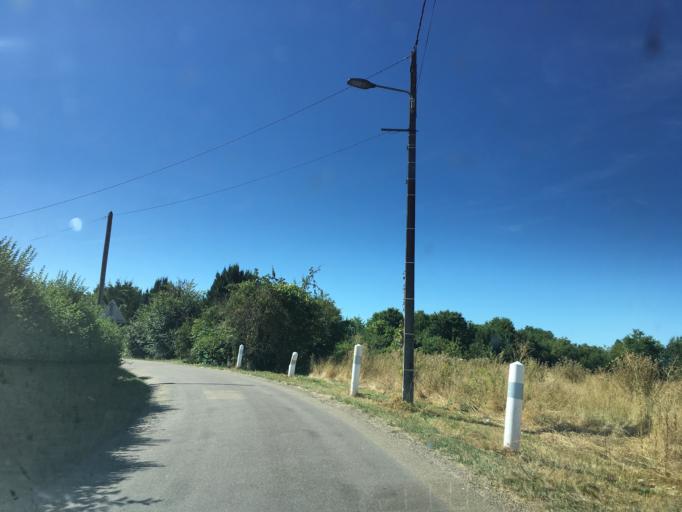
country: FR
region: Bourgogne
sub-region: Departement de l'Yonne
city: Fleury-la-Vallee
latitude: 47.8906
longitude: 3.4390
